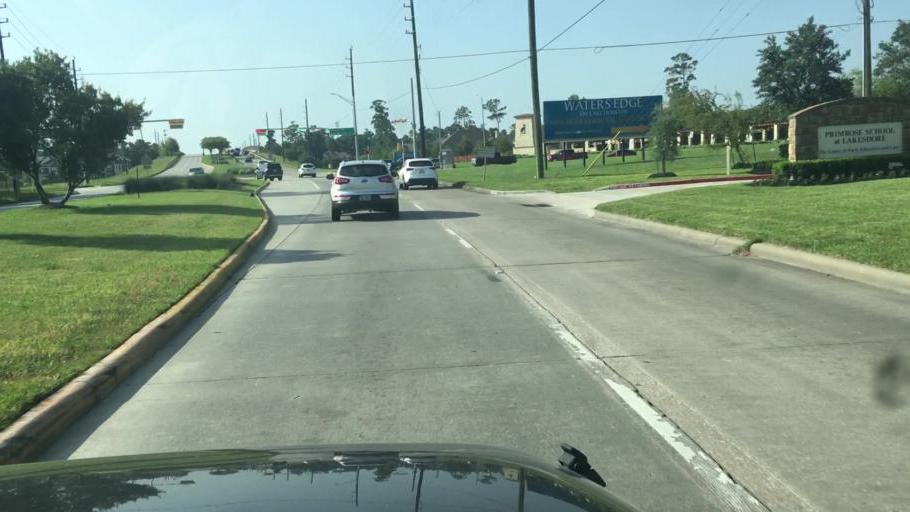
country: US
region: Texas
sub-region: Harris County
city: Atascocita
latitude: 29.9634
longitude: -95.1682
